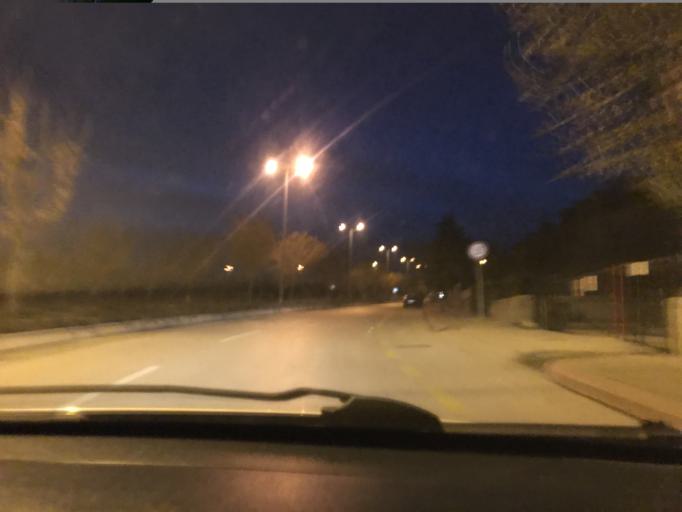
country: TR
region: Ankara
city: Batikent
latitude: 39.9598
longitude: 32.7474
